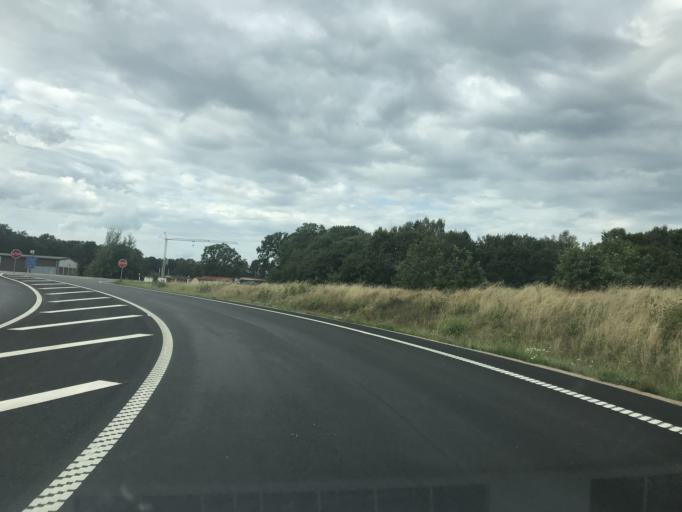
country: SE
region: Skane
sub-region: Hassleholms Kommun
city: Hassleholm
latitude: 56.1413
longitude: 13.8047
